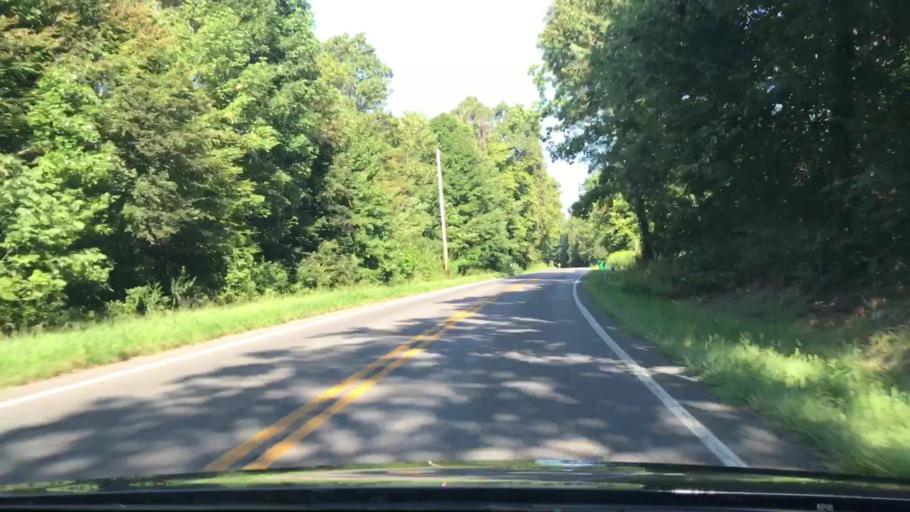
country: US
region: Kentucky
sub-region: Graves County
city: Mayfield
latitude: 36.7795
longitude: -88.5202
